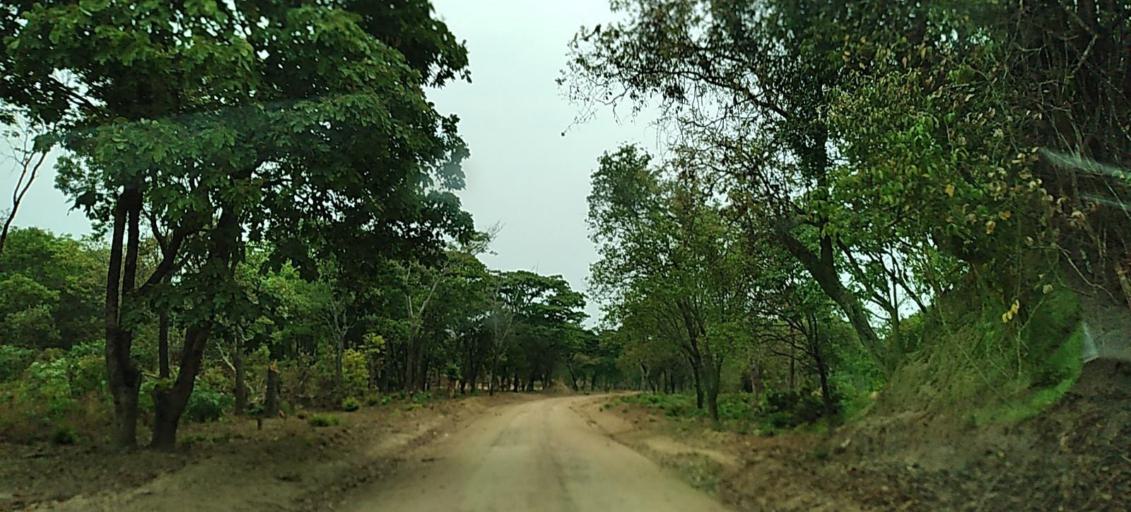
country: ZM
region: North-Western
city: Solwezi
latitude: -12.5439
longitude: 26.5279
